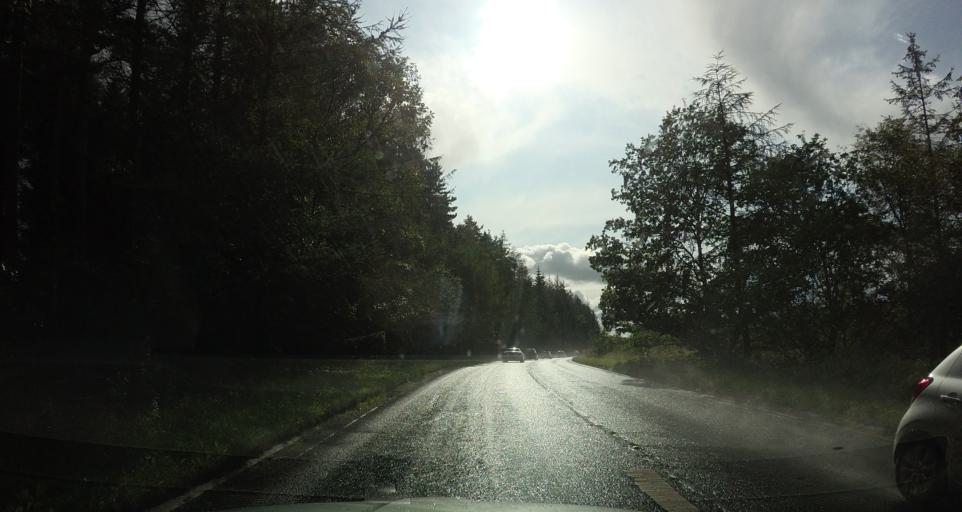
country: GB
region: Scotland
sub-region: Clackmannanshire
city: Dollar
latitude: 56.1233
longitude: -3.6919
